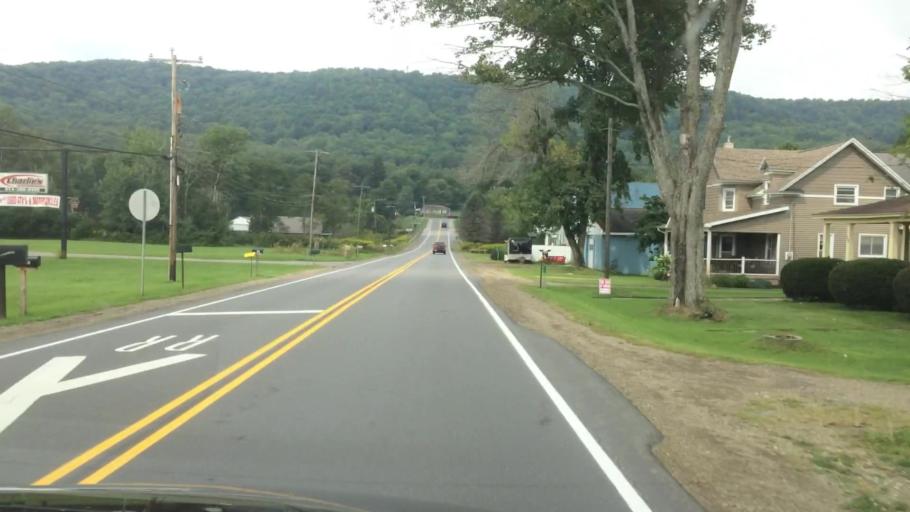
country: US
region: Pennsylvania
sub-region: McKean County
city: Bradford
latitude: 41.9139
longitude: -78.6463
